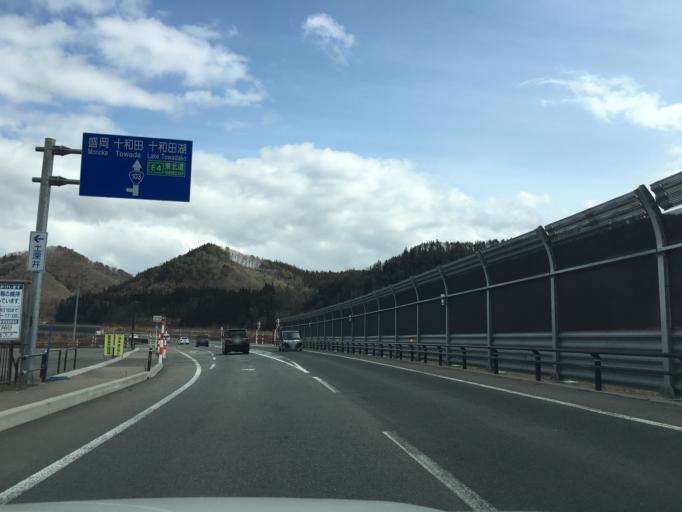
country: JP
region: Akita
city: Hanawa
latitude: 40.2237
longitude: 140.7178
